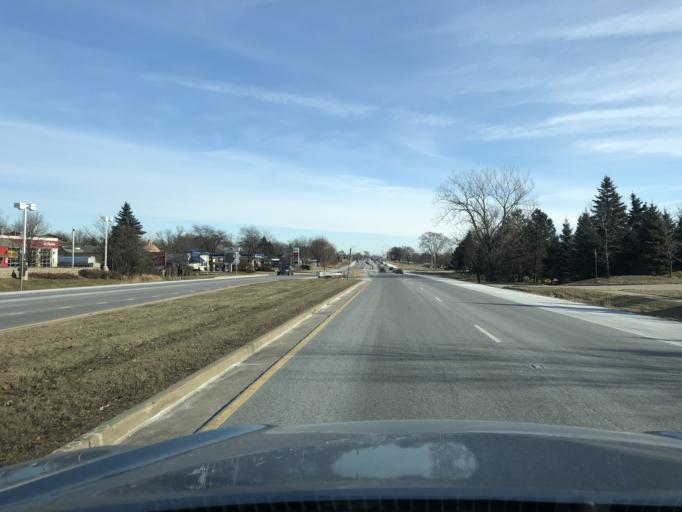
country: US
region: Illinois
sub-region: Lake County
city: Grandwood Park
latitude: 42.3859
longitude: -87.9937
